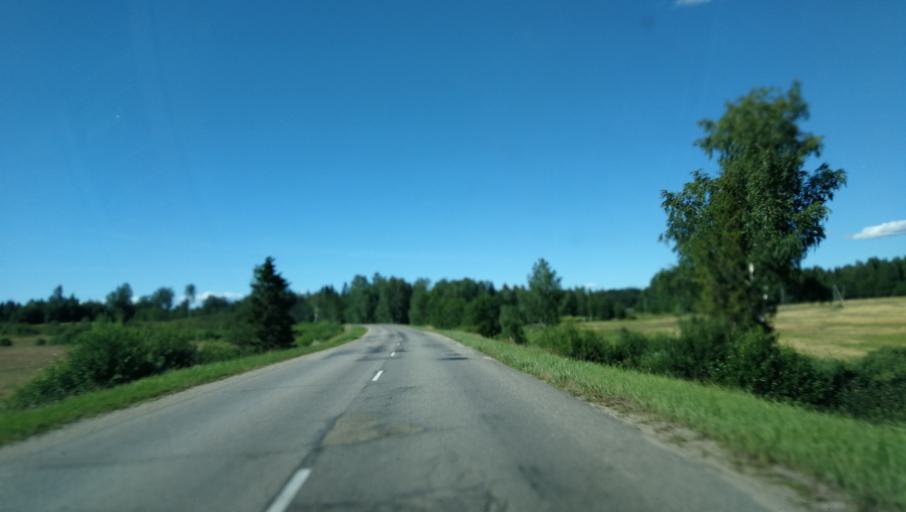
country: LV
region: Madonas Rajons
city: Madona
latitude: 56.9675
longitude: 26.0482
